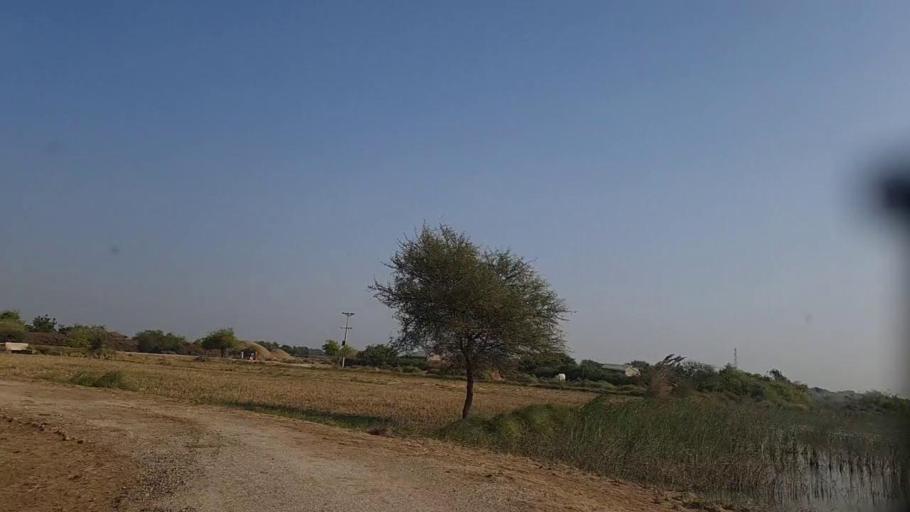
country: PK
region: Sindh
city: Jati
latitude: 24.5228
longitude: 68.2672
